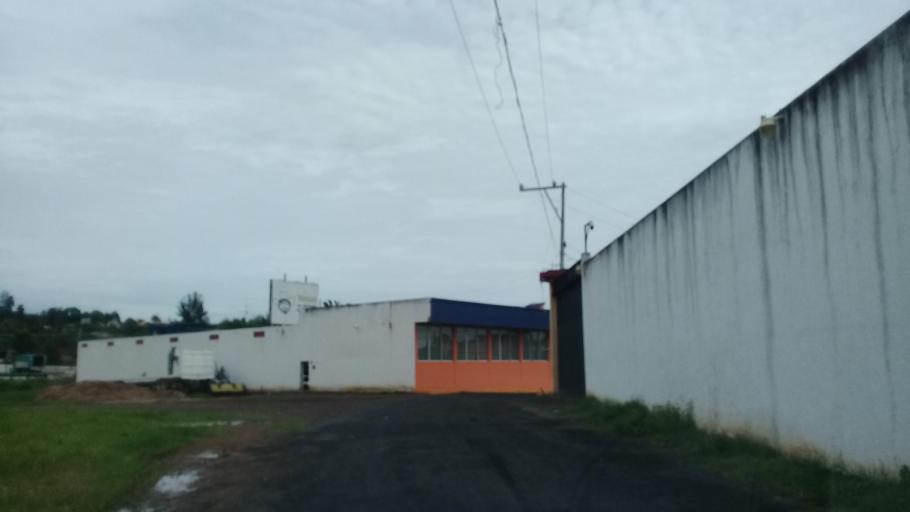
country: MX
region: Veracruz
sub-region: Emiliano Zapata
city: Dos Rios
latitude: 19.4852
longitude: -96.8059
